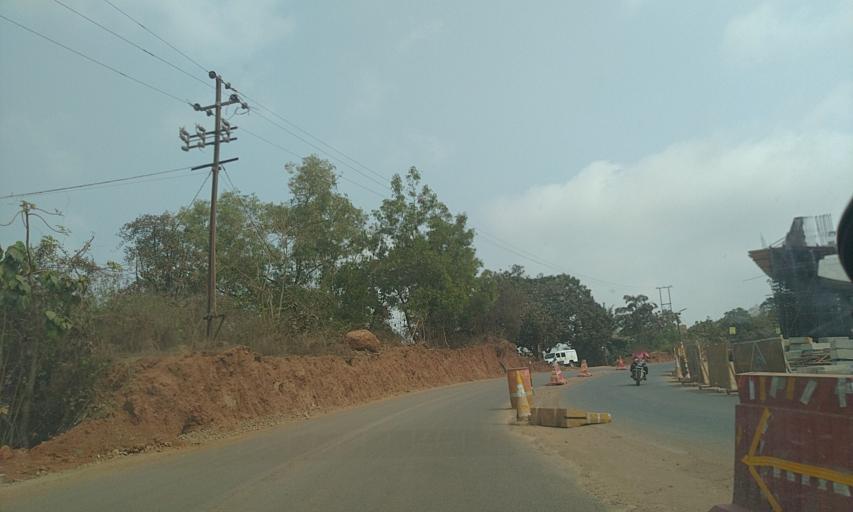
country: IN
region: Goa
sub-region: South Goa
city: Sancoale
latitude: 15.3871
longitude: 73.9206
